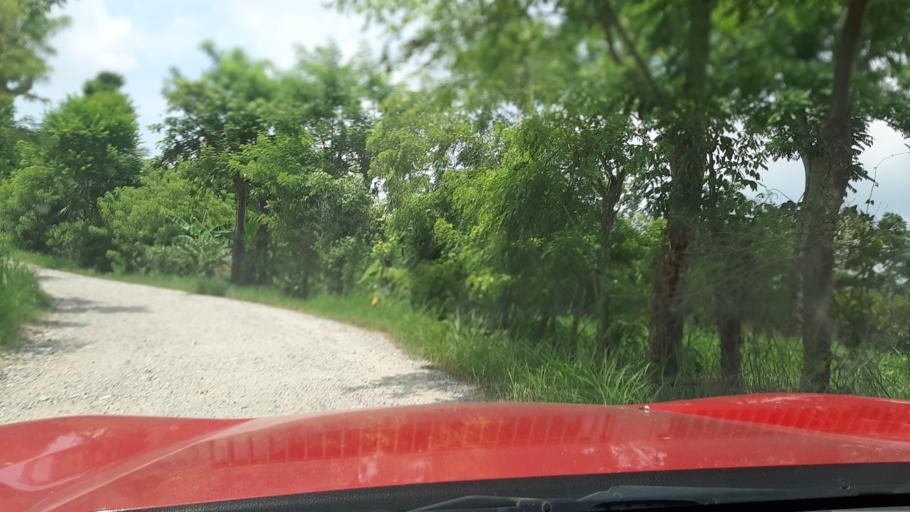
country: MX
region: Veracruz
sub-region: Papantla
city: Polutla
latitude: 20.4588
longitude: -97.2400
